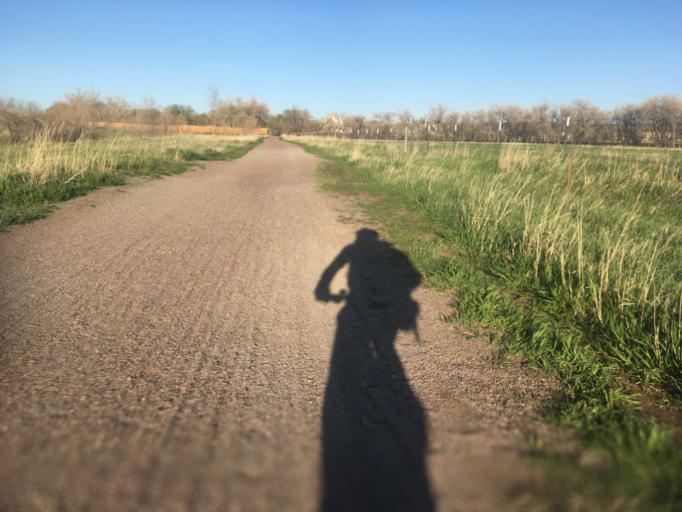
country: US
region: Colorado
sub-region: Boulder County
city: Lafayette
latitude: 39.9797
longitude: -105.0820
